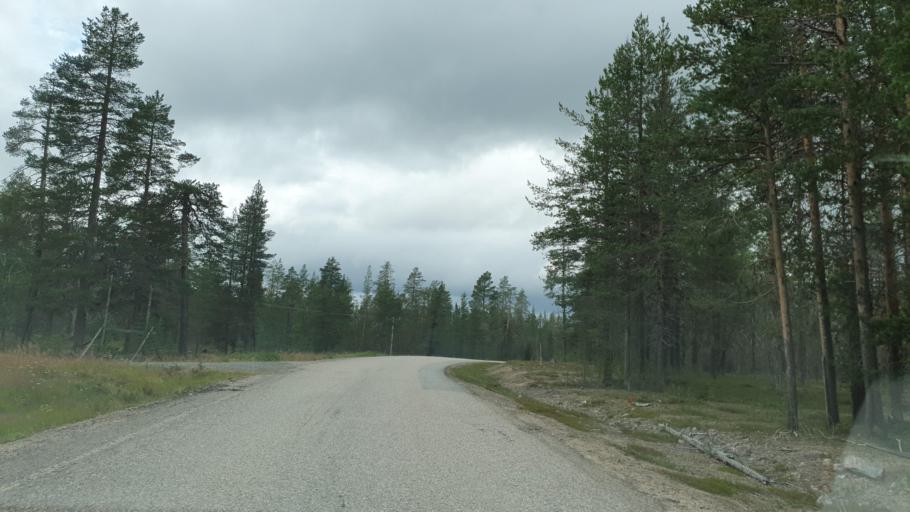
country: FI
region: Lapland
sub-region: Tunturi-Lappi
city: Kolari
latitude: 67.5187
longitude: 24.1956
